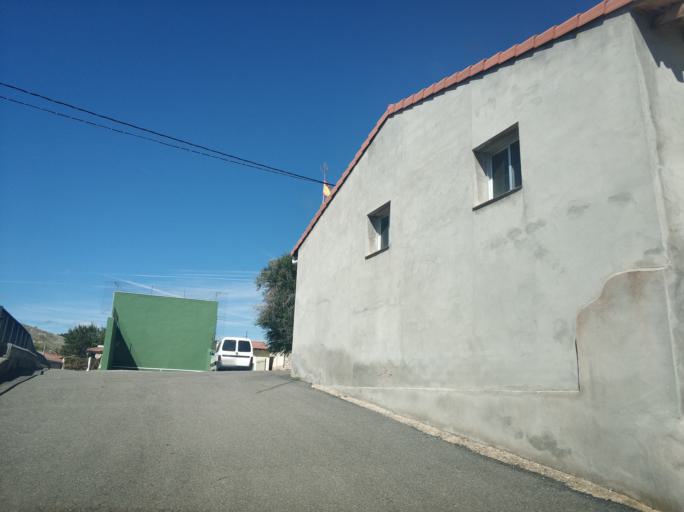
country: ES
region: Castille and Leon
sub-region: Provincia de Soria
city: Espeja de San Marcelino
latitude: 41.8026
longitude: -3.2216
